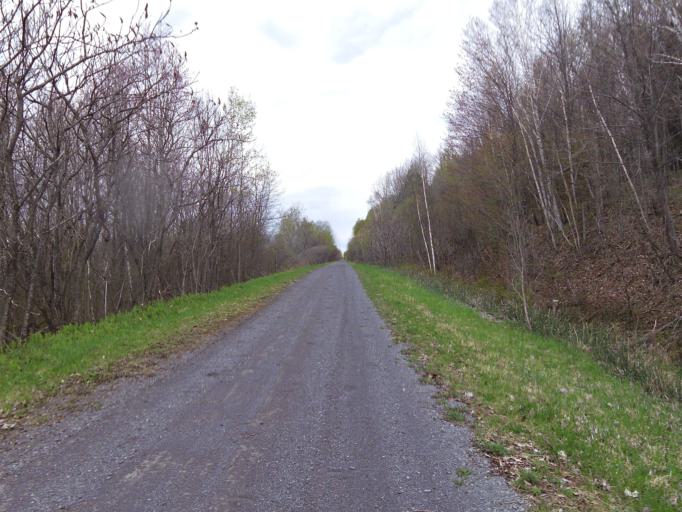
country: CA
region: Quebec
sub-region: Outaouais
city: Papineauville
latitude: 45.5172
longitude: -74.9457
